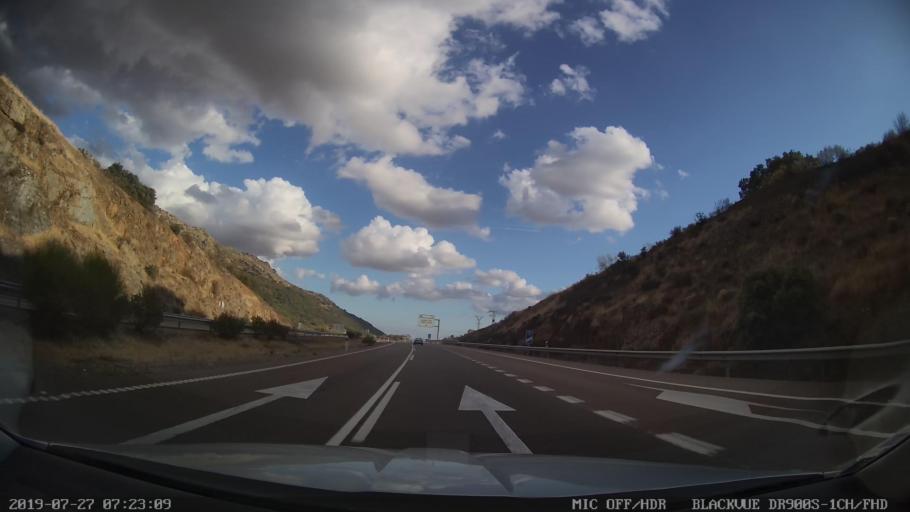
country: ES
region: Extremadura
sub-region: Provincia de Caceres
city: Puerto de Santa Cruz
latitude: 39.3265
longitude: -5.8583
